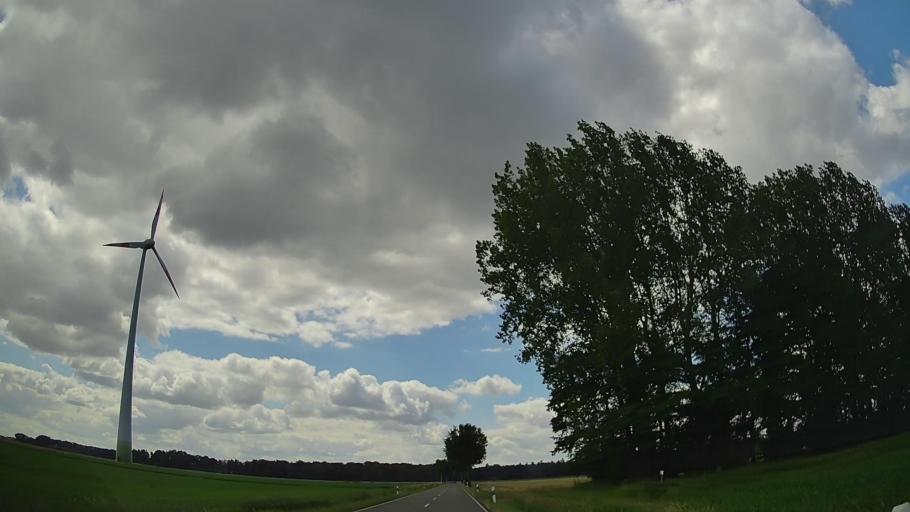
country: DE
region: Lower Saxony
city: Brockum
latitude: 52.5014
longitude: 8.4235
